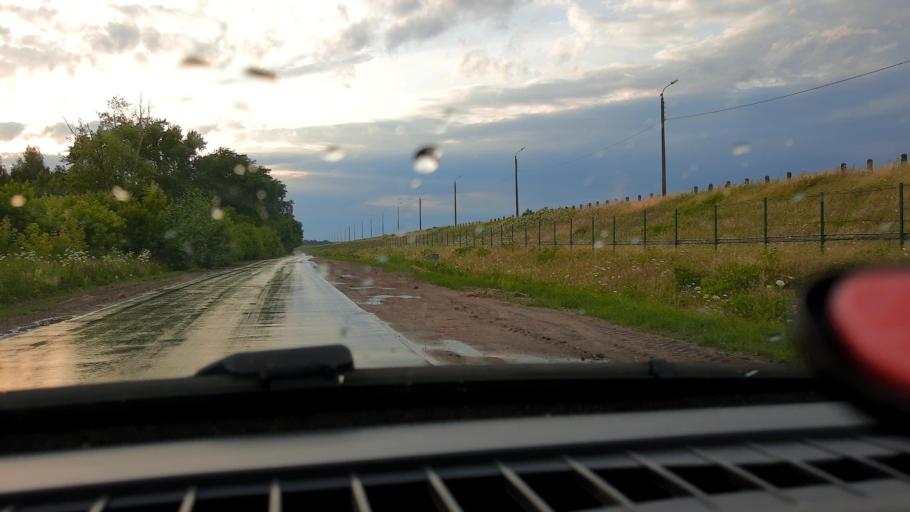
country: RU
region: Nizjnij Novgorod
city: Gorodets
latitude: 56.6635
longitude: 43.4353
